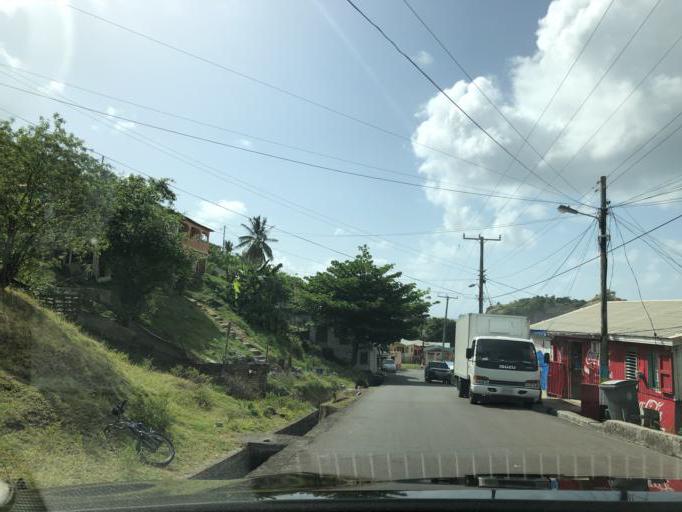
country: LC
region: Dennery Quarter
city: Dennery
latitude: 13.9138
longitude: -60.8873
